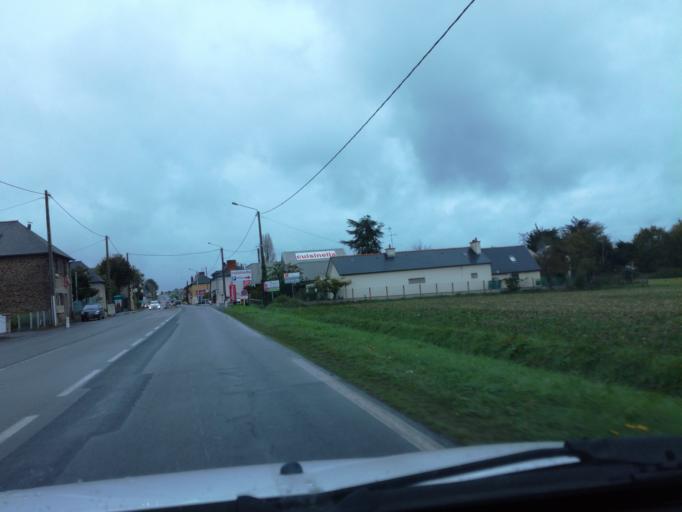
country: FR
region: Brittany
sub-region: Departement d'Ille-et-Vilaine
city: La Chapelle-des-Fougeretz
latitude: 48.1760
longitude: -1.7217
